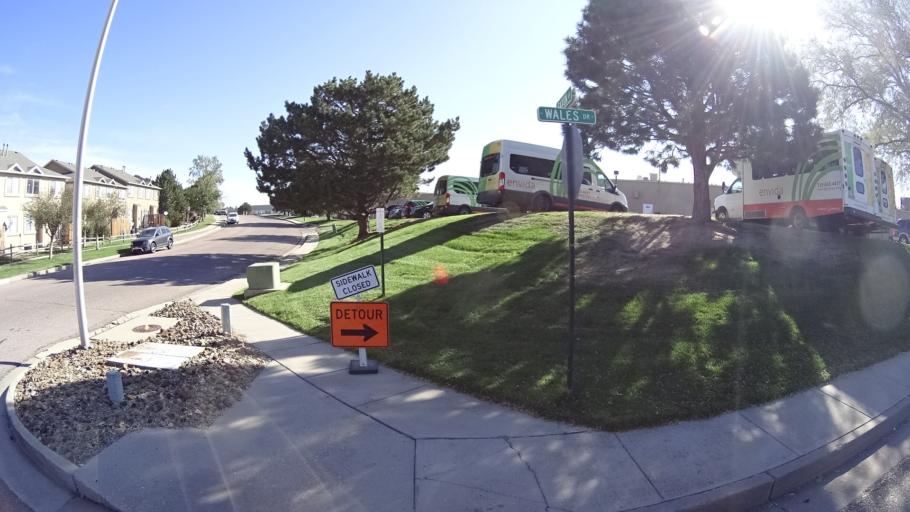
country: US
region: Colorado
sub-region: El Paso County
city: Colorado Springs
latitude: 38.9130
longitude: -104.7904
